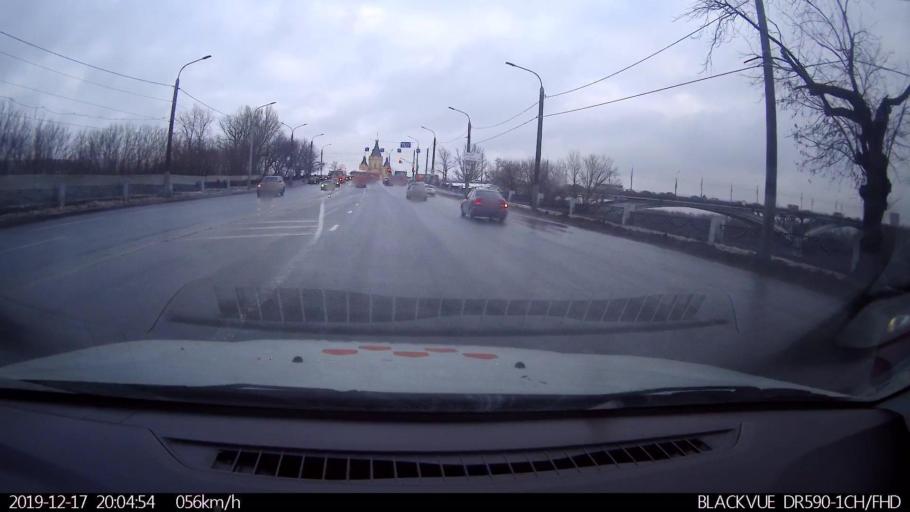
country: RU
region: Nizjnij Novgorod
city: Nizhniy Novgorod
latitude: 56.3273
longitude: 43.9682
